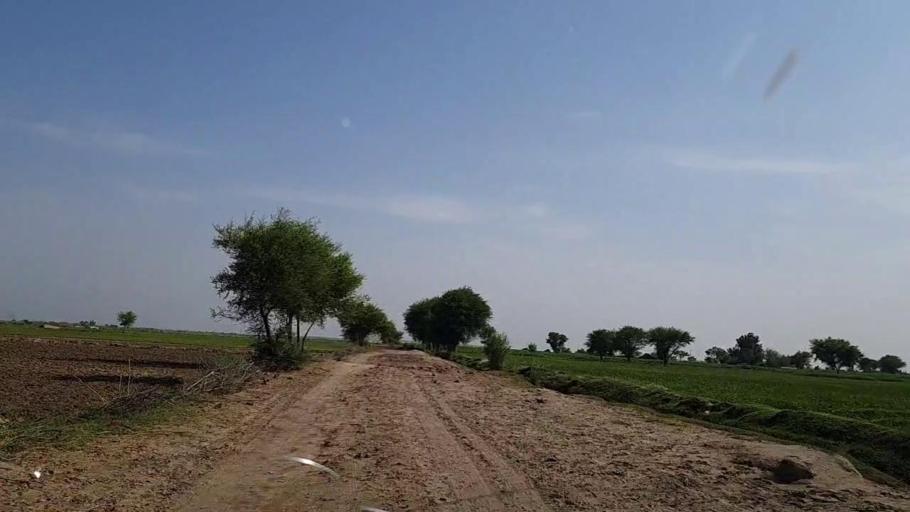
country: PK
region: Sindh
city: Khanpur
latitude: 27.6911
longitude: 69.3674
